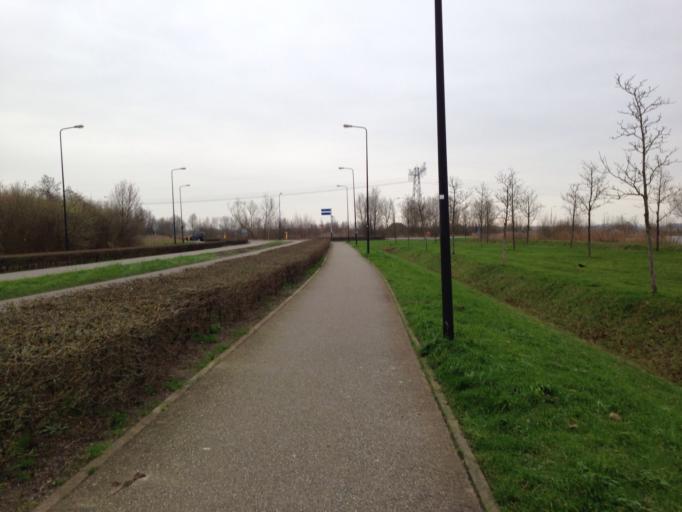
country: NL
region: Gelderland
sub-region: Gemeente Maasdriel
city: Hedel
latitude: 51.7227
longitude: 5.2465
